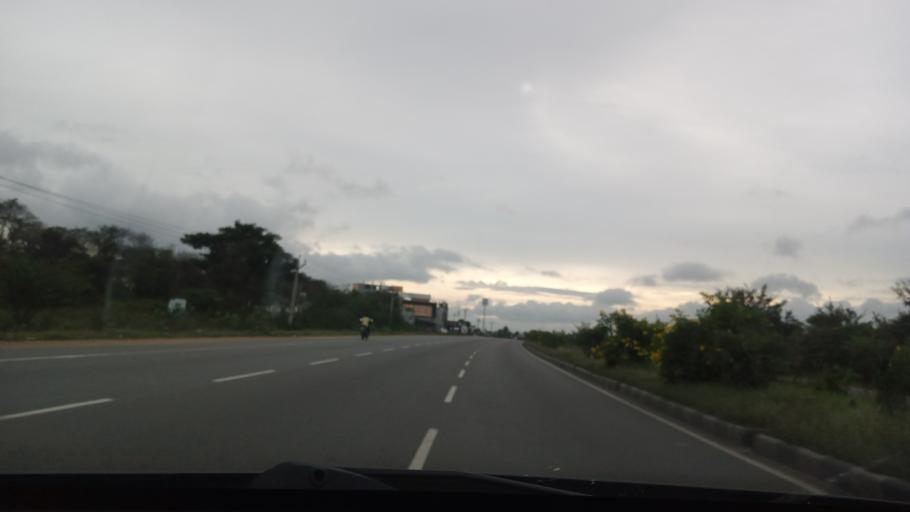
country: IN
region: Tamil Nadu
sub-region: Vellore
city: Vaniyambadi
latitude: 12.6574
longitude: 78.6051
